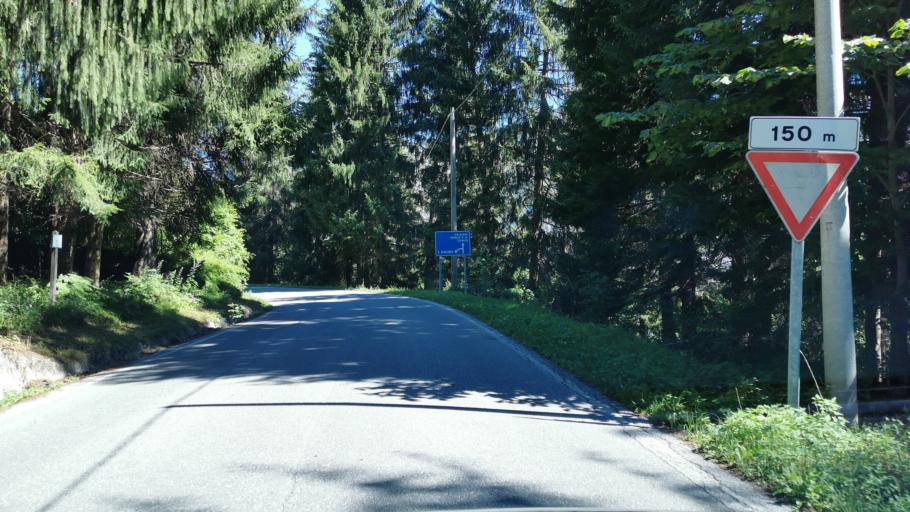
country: IT
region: Piedmont
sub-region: Provincia di Cuneo
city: Entracque
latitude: 44.2298
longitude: 7.3898
